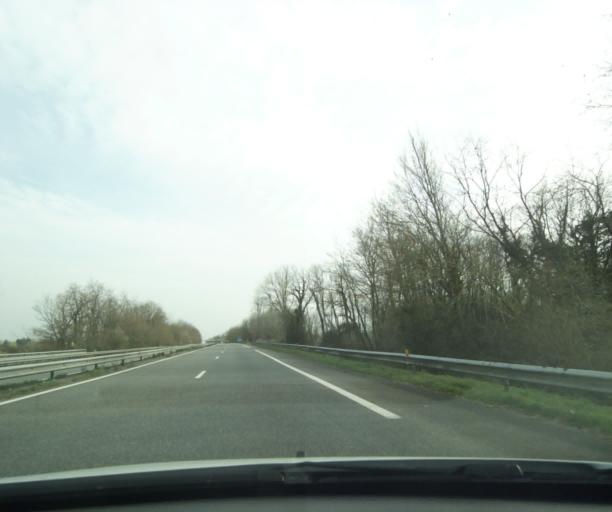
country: FR
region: Aquitaine
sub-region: Departement des Pyrenees-Atlantiques
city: Orthez
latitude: 43.4924
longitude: -0.8233
